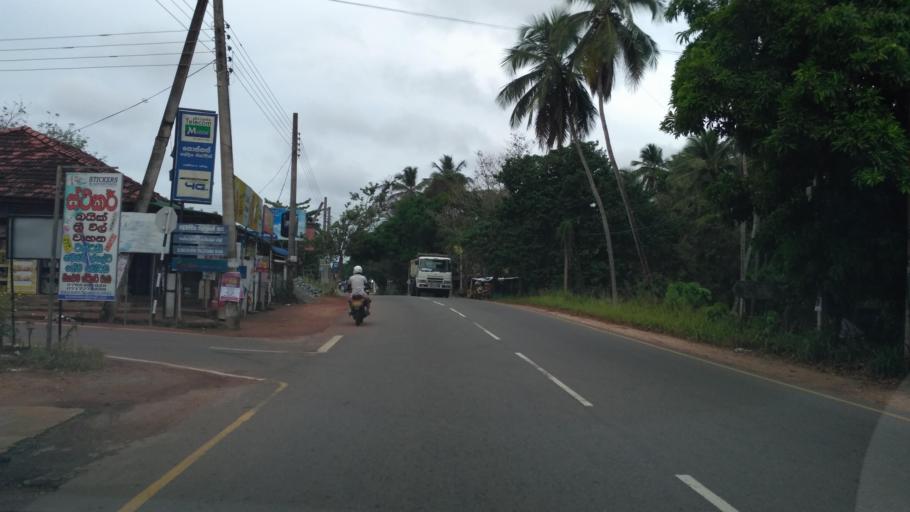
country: LK
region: North Western
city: Kuliyapitiya
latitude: 7.3272
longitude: 80.0515
